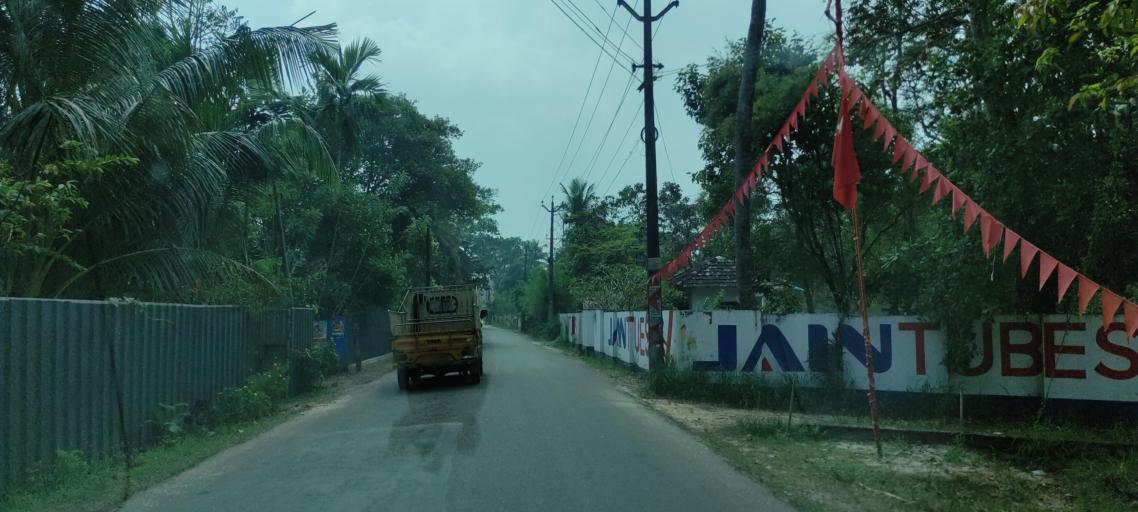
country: IN
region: Kerala
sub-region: Alappuzha
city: Shertallai
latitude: 9.6173
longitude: 76.3479
